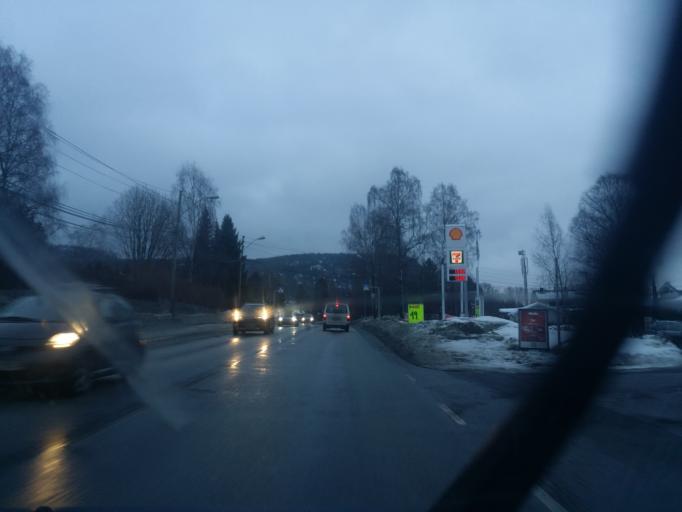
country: NO
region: Akershus
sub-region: Baerum
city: Skui
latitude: 59.9235
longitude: 10.4770
